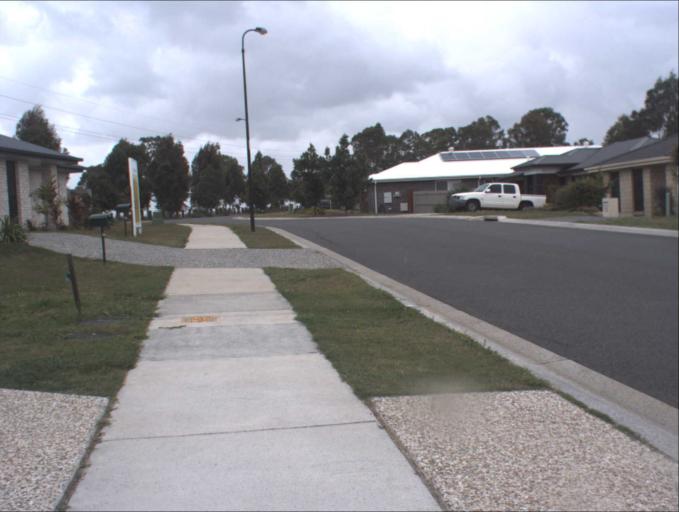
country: AU
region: Queensland
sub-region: Logan
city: Waterford West
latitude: -27.7118
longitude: 153.1157
